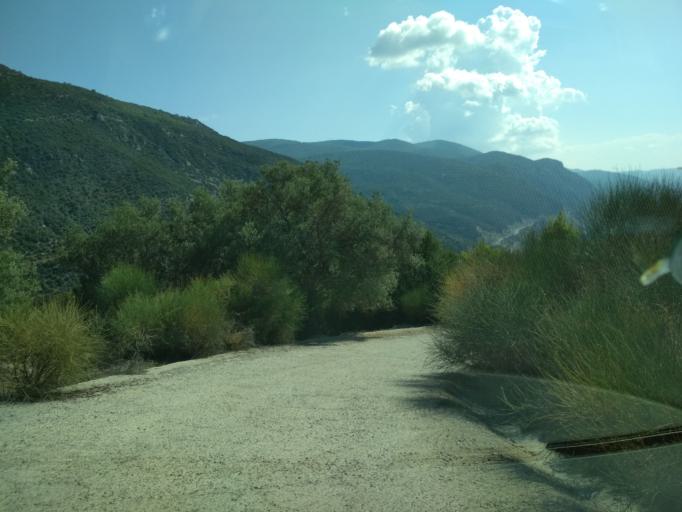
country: GR
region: Central Greece
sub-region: Nomos Evvoias
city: Oreoi
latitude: 38.8528
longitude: 23.1160
